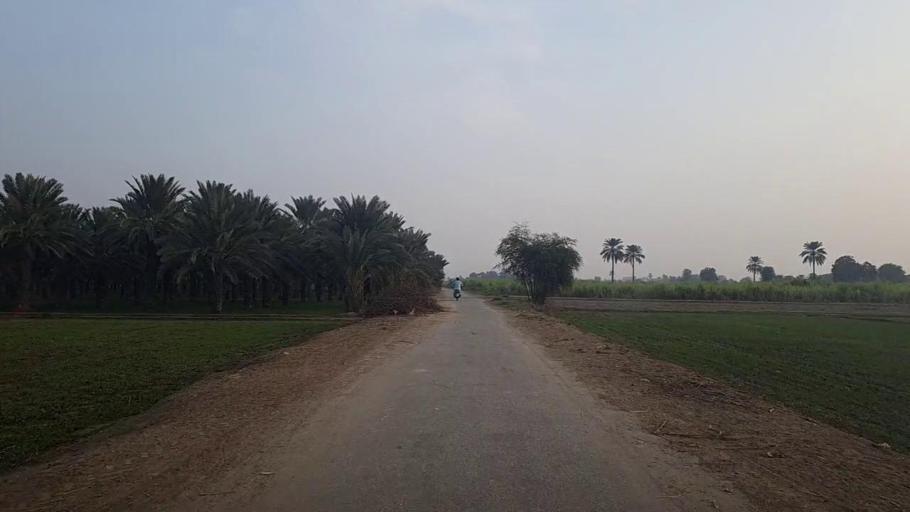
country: PK
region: Sindh
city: Kot Diji
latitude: 27.3830
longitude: 68.6622
